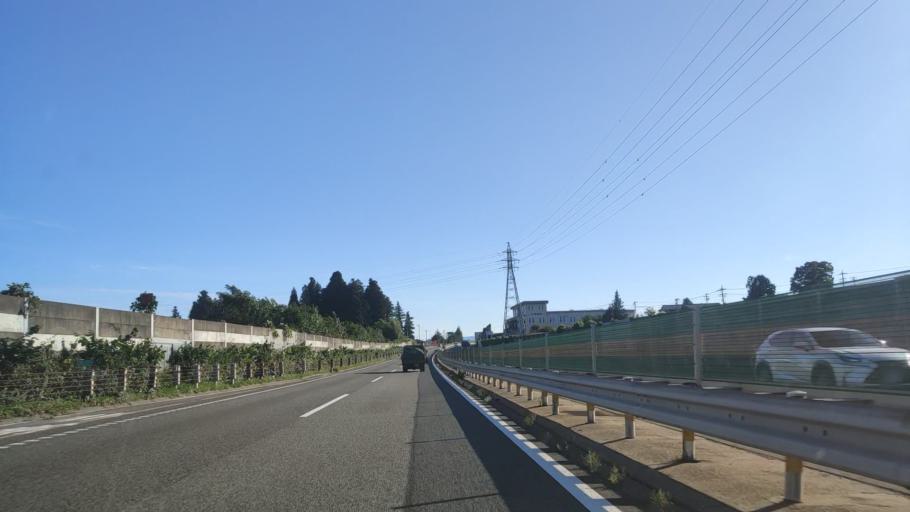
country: JP
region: Nagano
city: Iida
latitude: 35.5131
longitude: 137.8020
